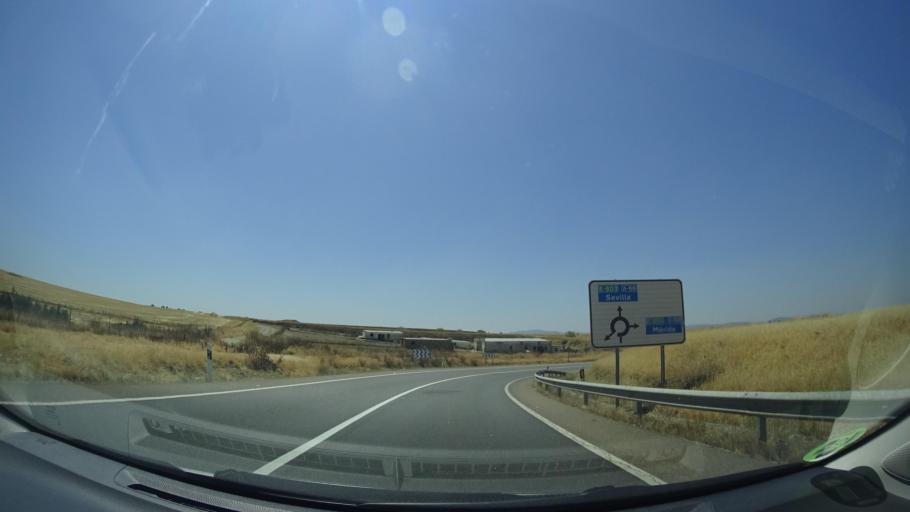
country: ES
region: Extremadura
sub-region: Provincia de Badajoz
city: Fuente de Cantos
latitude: 38.2315
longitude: -6.2932
